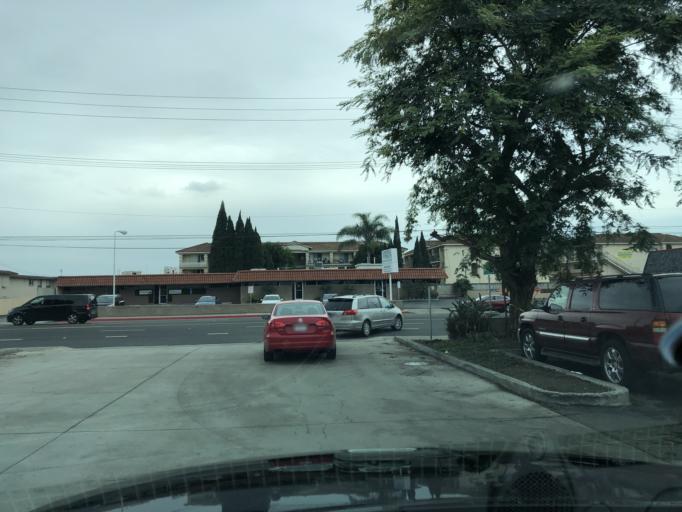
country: US
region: California
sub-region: Orange County
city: Westminster
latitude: 33.7304
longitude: -118.0227
